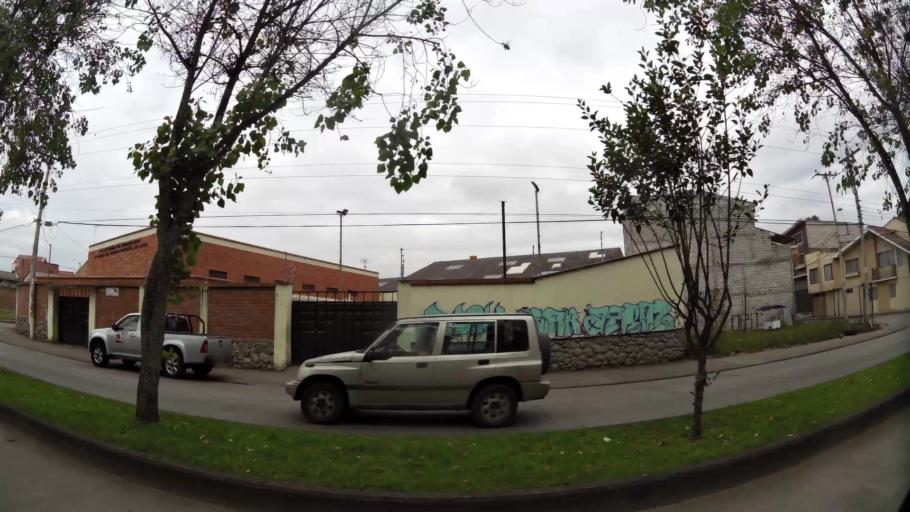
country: EC
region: Azuay
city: Cuenca
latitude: -2.9040
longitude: -78.9811
